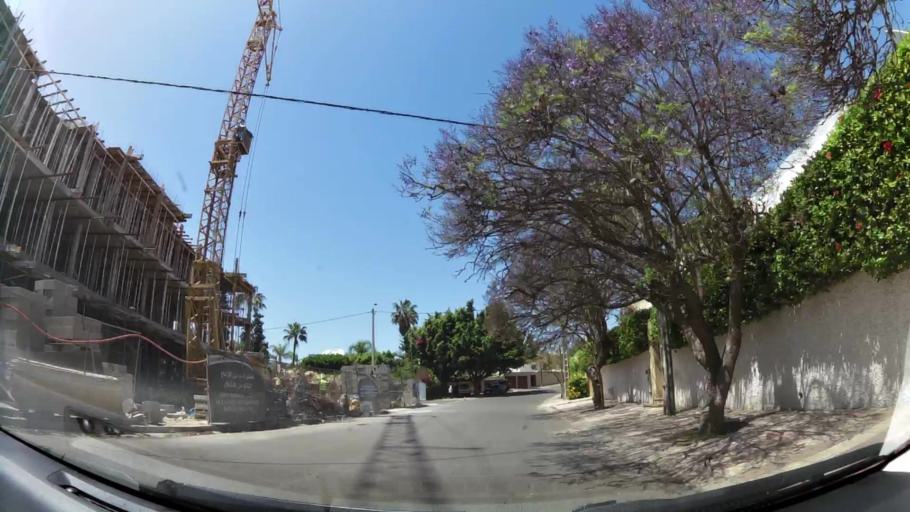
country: MA
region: Souss-Massa-Draa
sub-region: Agadir-Ida-ou-Tnan
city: Agadir
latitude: 30.4265
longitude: -9.5994
